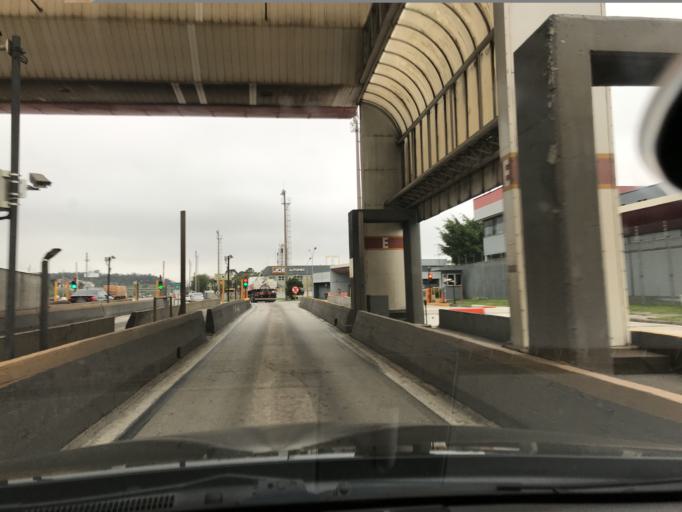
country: BR
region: Sao Paulo
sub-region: Carapicuiba
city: Carapicuiba
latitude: -23.5107
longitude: -46.8176
